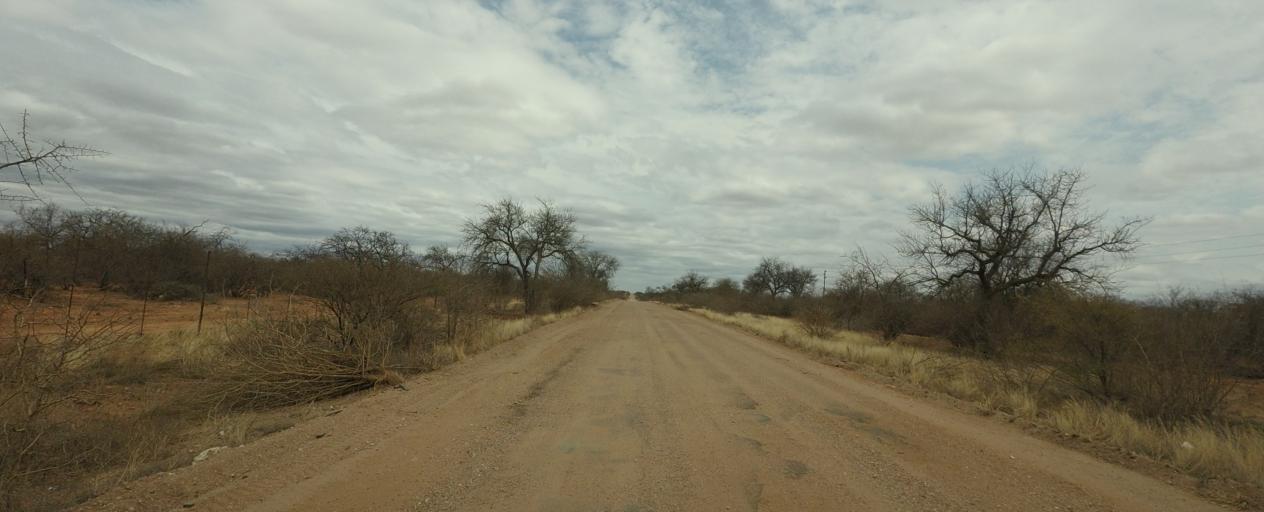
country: BW
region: Central
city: Mathathane
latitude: -22.6721
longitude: 28.6801
